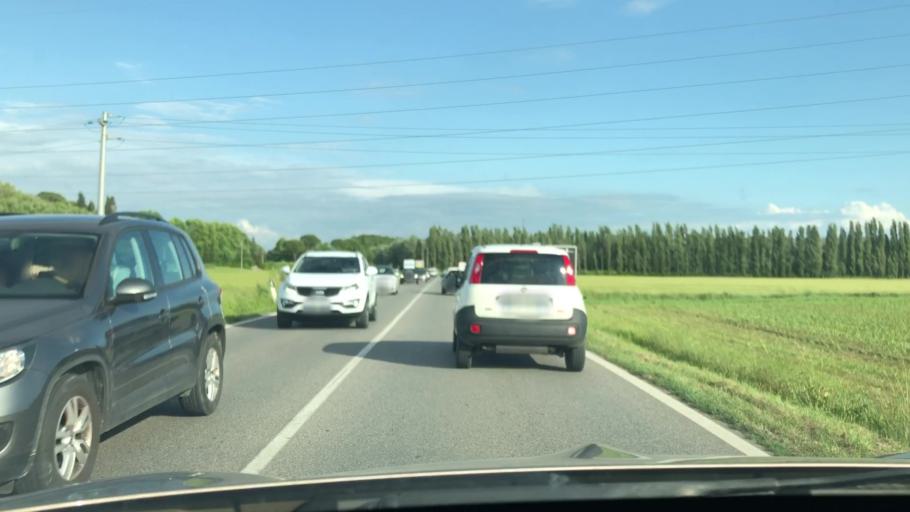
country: IT
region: Tuscany
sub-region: Province of Pisa
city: Treggiaia
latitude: 43.6176
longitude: 10.6758
